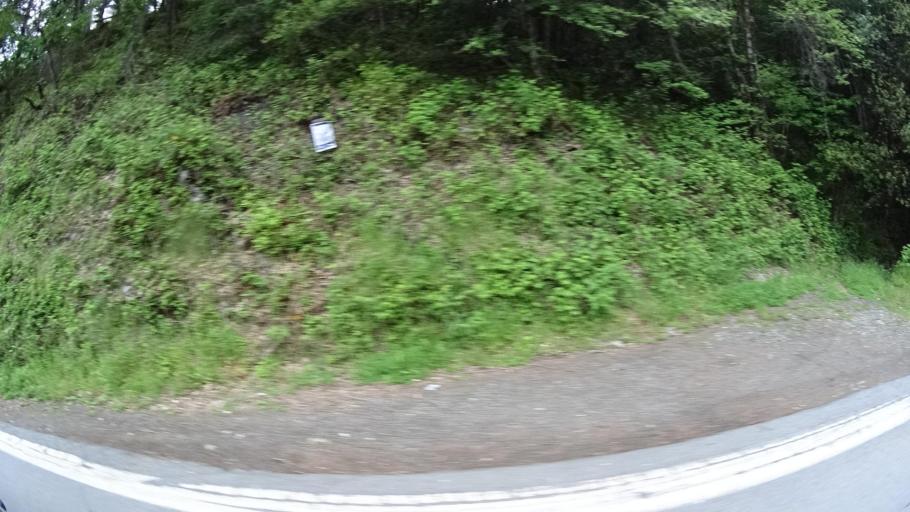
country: US
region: California
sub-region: Humboldt County
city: Willow Creek
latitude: 41.1921
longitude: -123.7144
